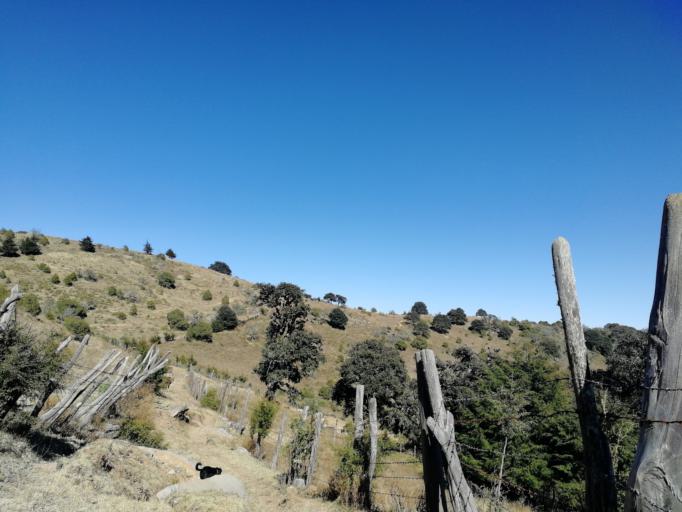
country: MX
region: San Luis Potosi
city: Zaragoza
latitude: 22.0050
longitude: -100.6104
